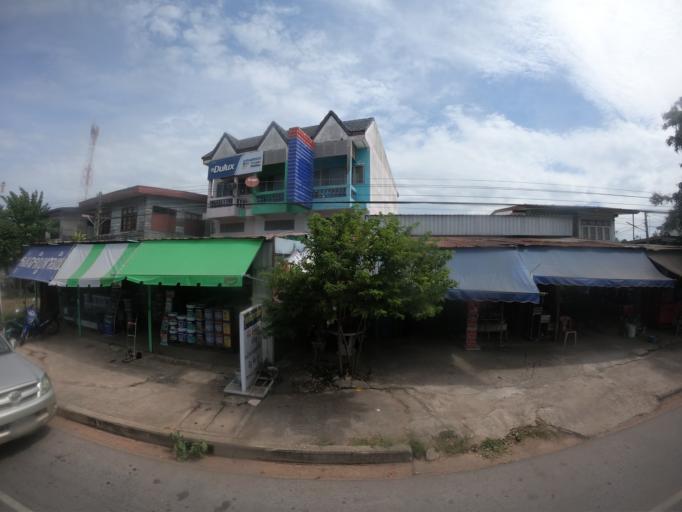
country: TH
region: Maha Sarakham
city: Chiang Yuen
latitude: 16.4053
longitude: 103.0988
